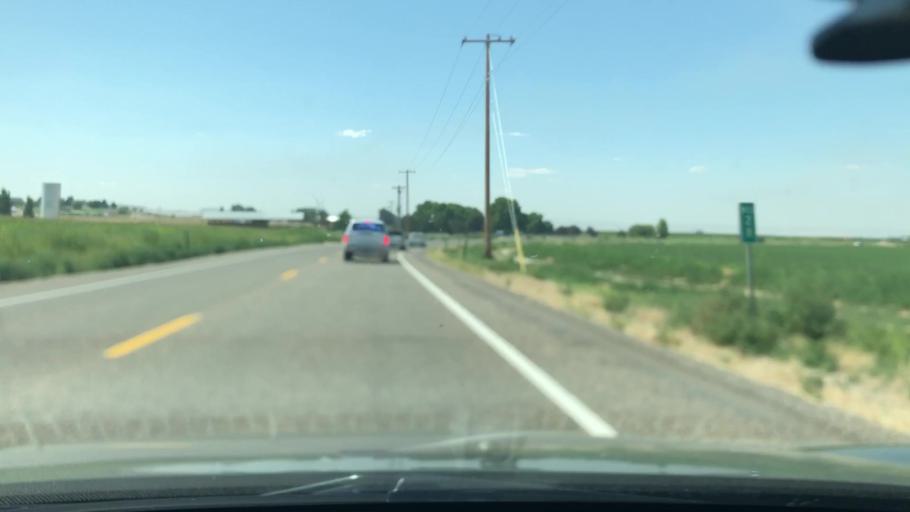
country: US
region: Idaho
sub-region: Owyhee County
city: Marsing
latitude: 43.5453
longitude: -116.8864
